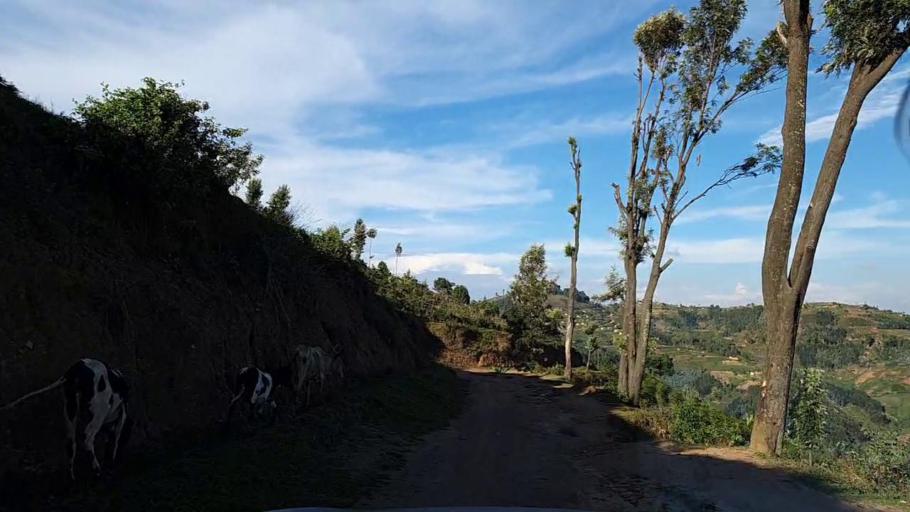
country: RW
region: Southern Province
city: Gikongoro
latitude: -2.4118
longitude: 29.5209
